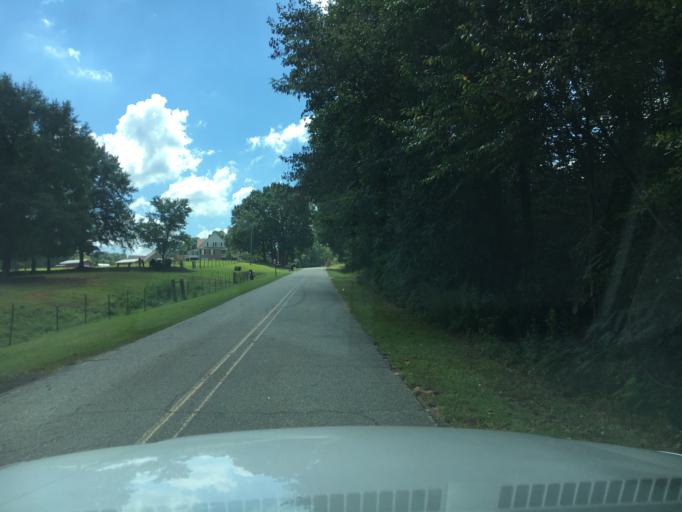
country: US
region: South Carolina
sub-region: Spartanburg County
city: Wellford
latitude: 34.8971
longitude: -82.0566
